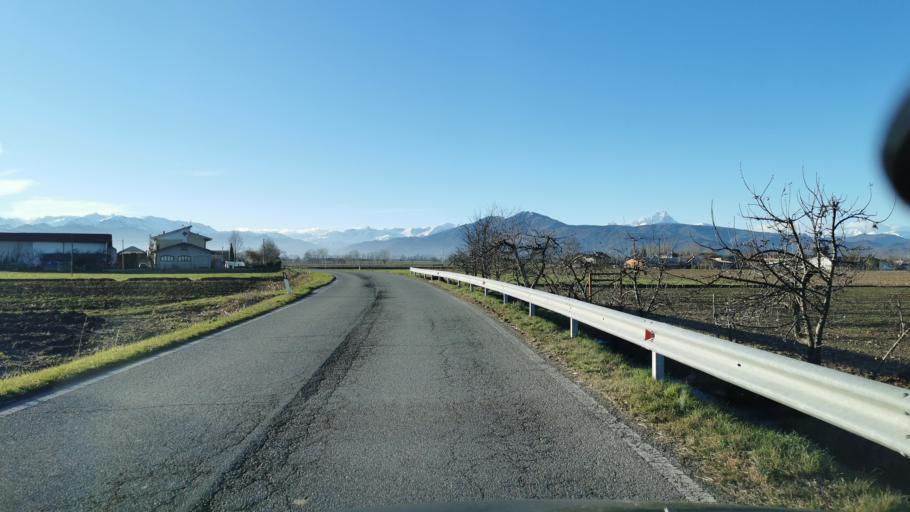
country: IT
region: Piedmont
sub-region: Provincia di Cuneo
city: Roata Rossi
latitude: 44.4577
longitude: 7.5140
